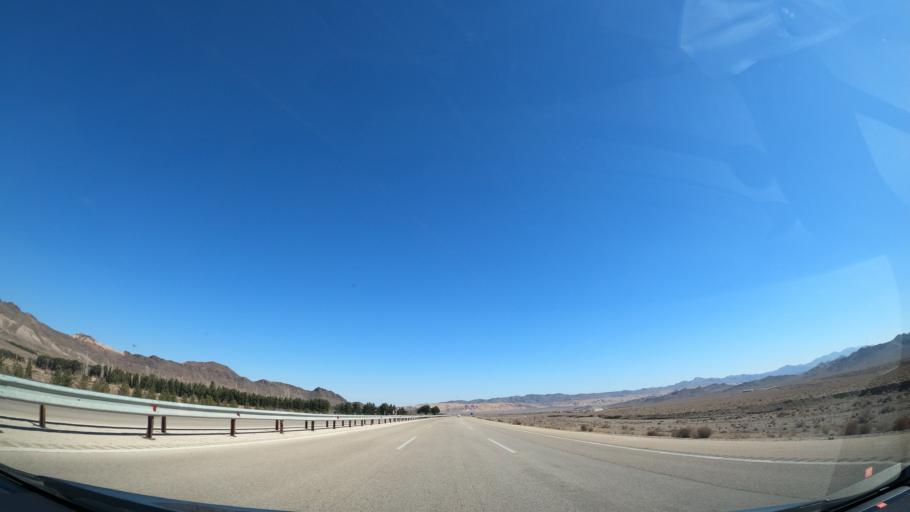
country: IR
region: Isfahan
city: Natanz
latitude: 33.3907
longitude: 51.9540
